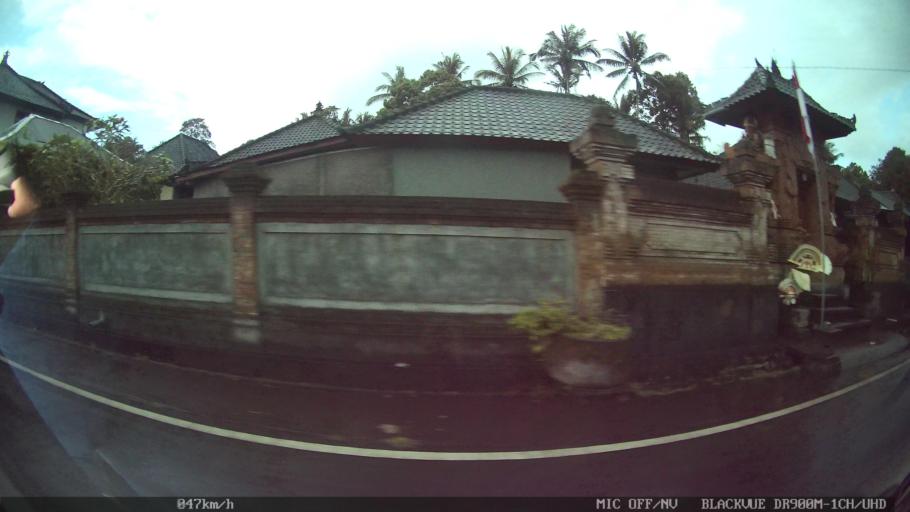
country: ID
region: Bali
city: Banjar Teguan
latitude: -8.5077
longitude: 115.2302
